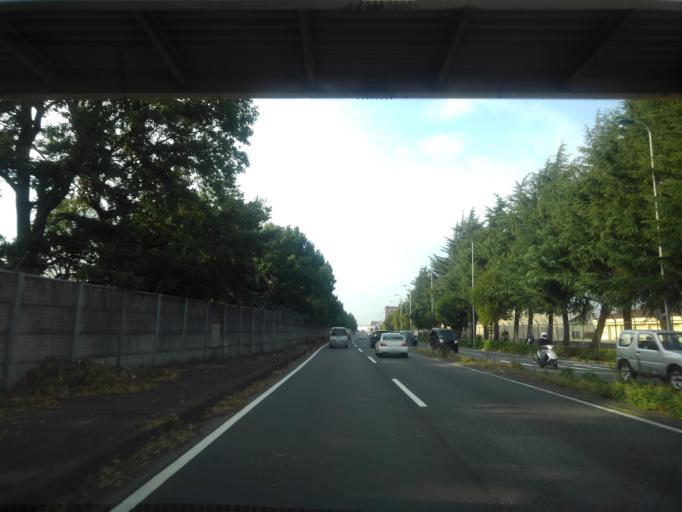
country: JP
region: Tokyo
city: Fussa
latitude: 35.7526
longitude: 139.3401
